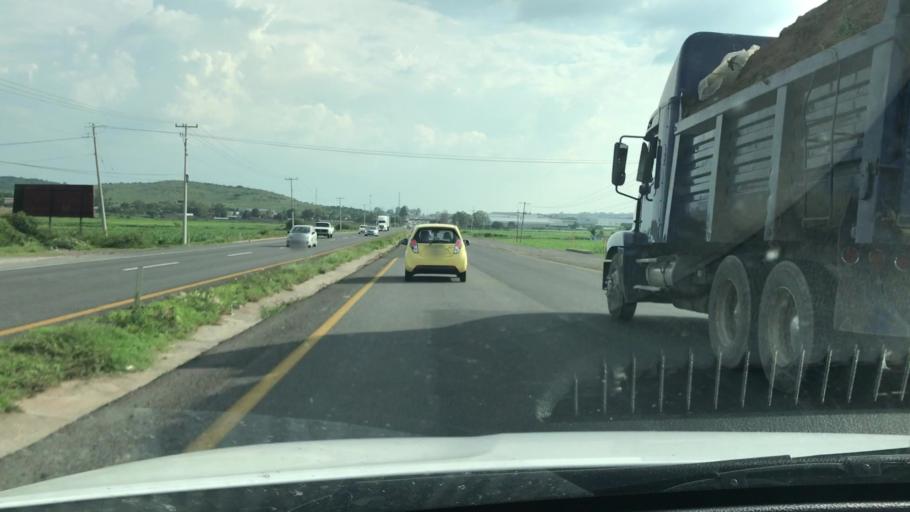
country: MX
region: Guanajuato
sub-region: Irapuato
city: Colonia Morelos de Guadalupe de Rivera
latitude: 20.5769
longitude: -101.4388
